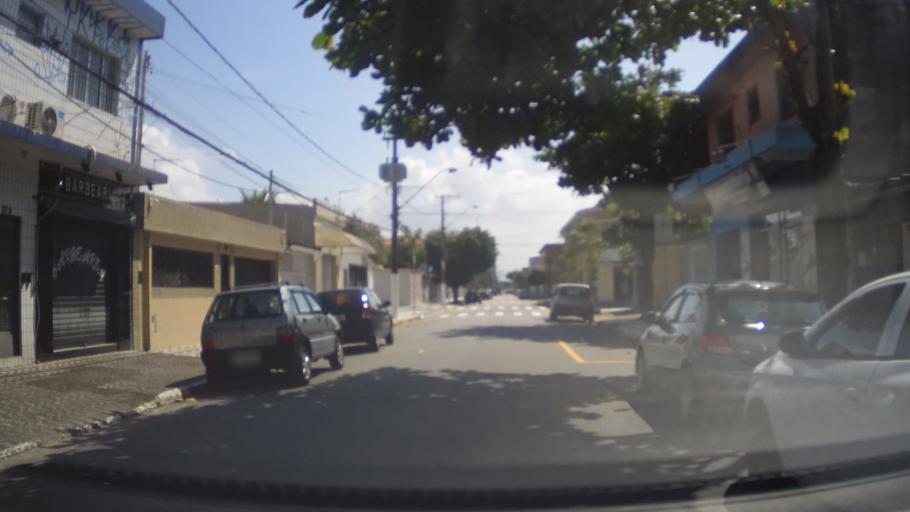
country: BR
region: Sao Paulo
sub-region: Praia Grande
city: Praia Grande
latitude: -24.0063
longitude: -46.4150
